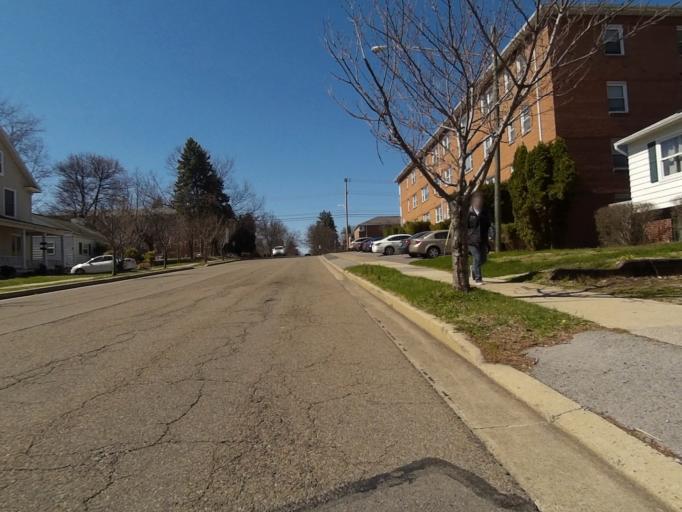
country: US
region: Pennsylvania
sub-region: Centre County
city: State College
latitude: 40.7909
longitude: -77.8523
